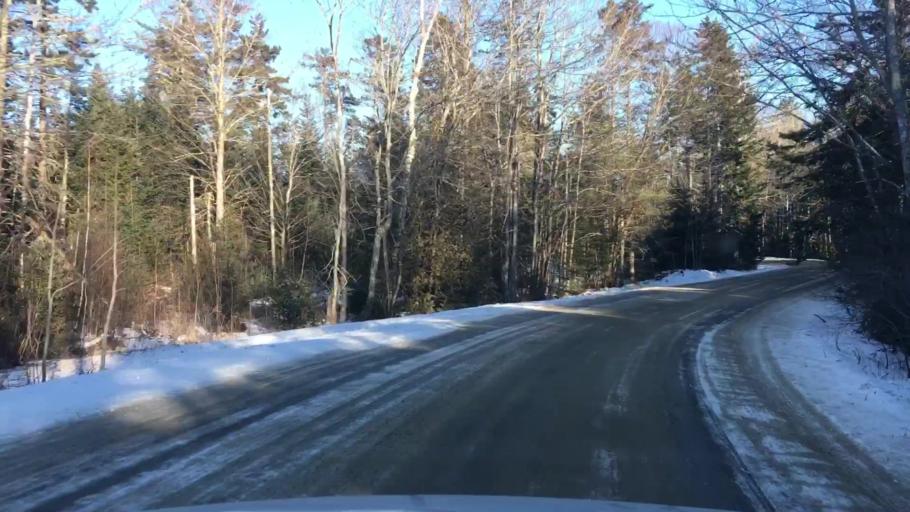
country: US
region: Maine
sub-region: Hancock County
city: Castine
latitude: 44.3833
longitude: -68.7472
